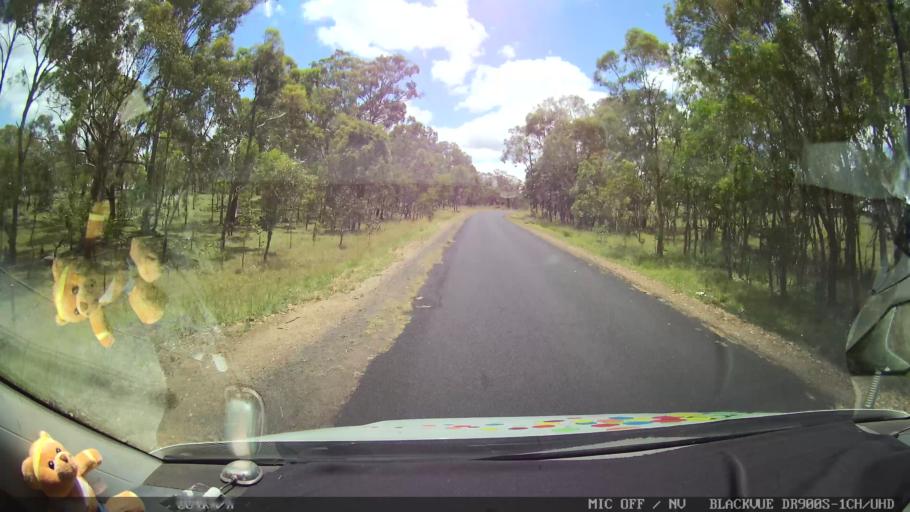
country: AU
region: New South Wales
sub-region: Glen Innes Severn
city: Glen Innes
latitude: -29.4328
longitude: 151.6851
